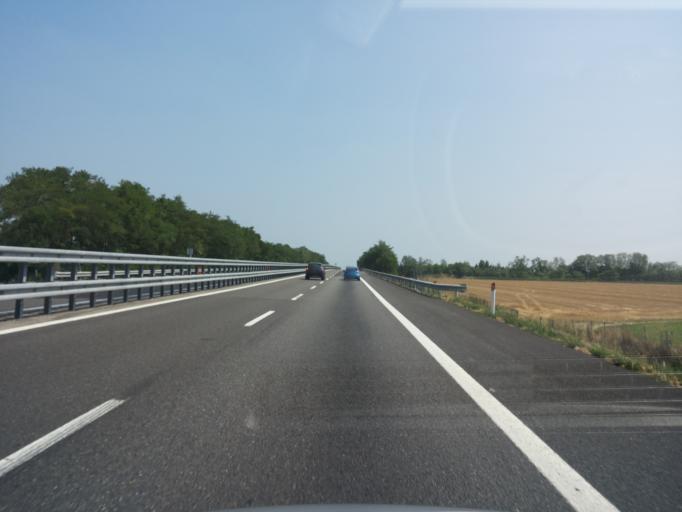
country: IT
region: Piedmont
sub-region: Provincia di Alessandria
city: Pontecurone
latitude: 44.9702
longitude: 8.9314
